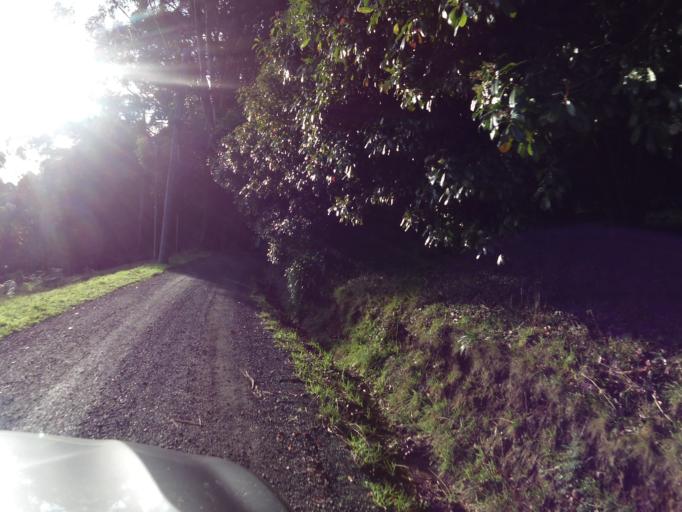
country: AU
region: Victoria
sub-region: Yarra Ranges
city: Ferny Creek
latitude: -37.8717
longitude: 145.3399
